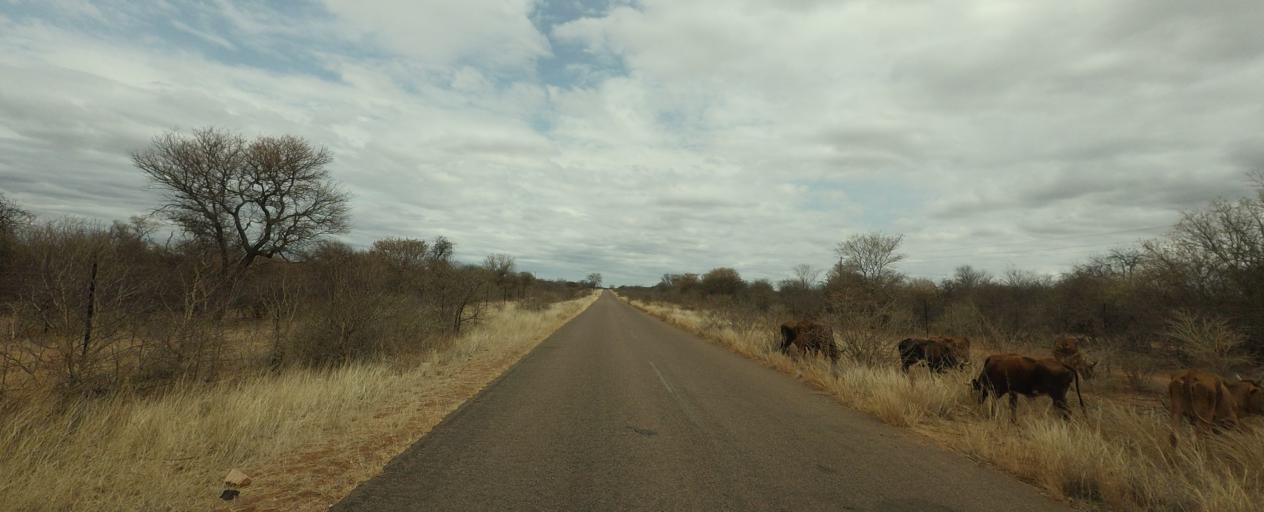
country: BW
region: Central
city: Mathathane
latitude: -22.6631
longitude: 28.7023
